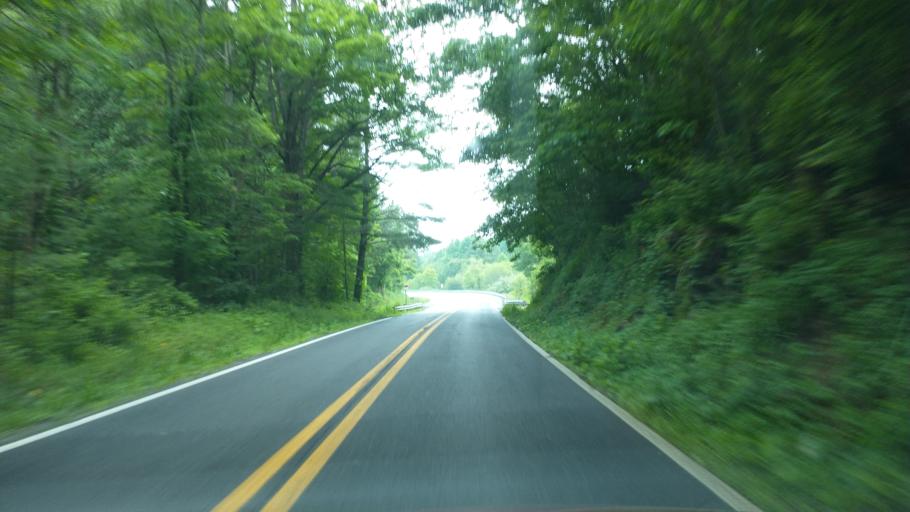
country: US
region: West Virginia
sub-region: Mercer County
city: Athens
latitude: 37.4161
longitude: -81.0553
